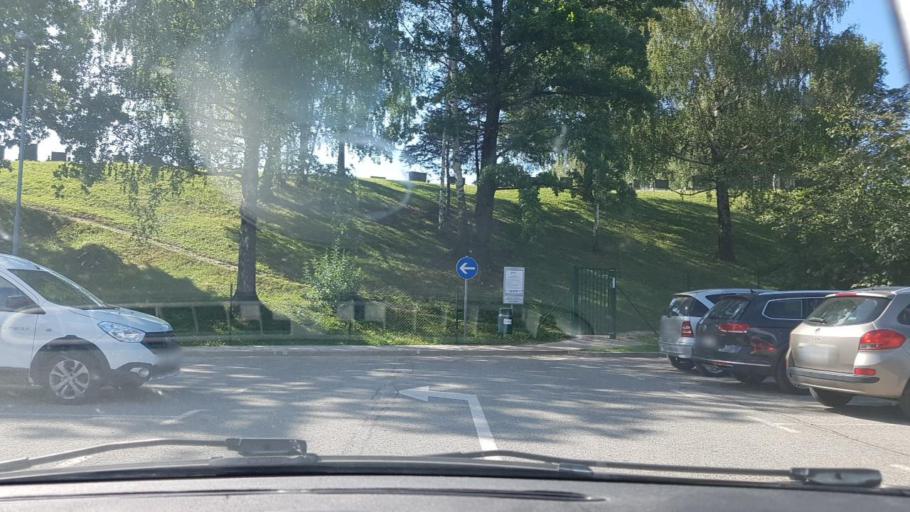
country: SI
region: Bled
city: Zasip
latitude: 46.4066
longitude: 14.1064
